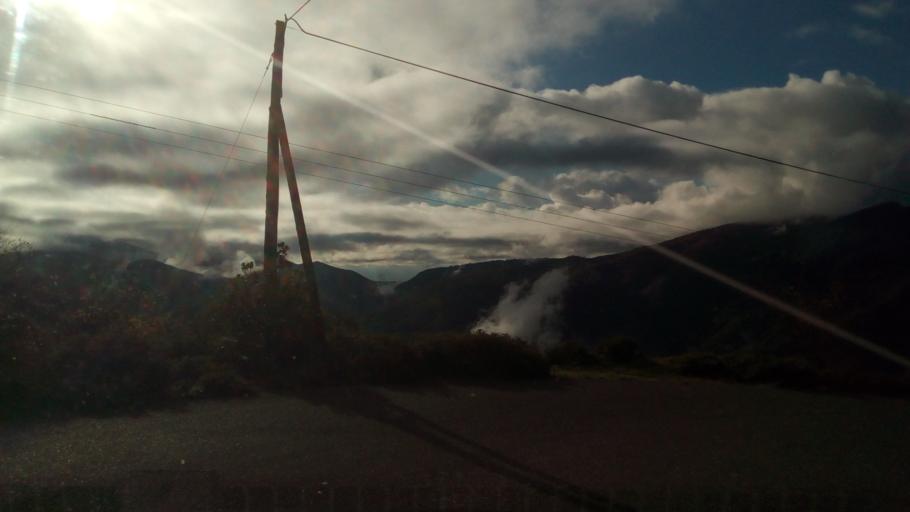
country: GR
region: West Greece
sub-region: Nomos Aitolias kai Akarnanias
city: Nafpaktos
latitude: 38.5153
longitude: 21.9629
